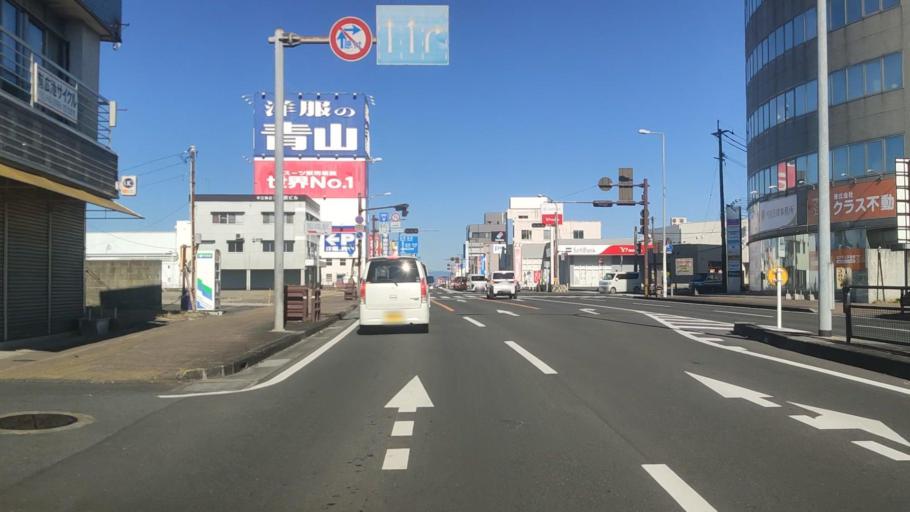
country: JP
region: Miyazaki
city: Miyakonojo
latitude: 31.7314
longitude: 131.0683
